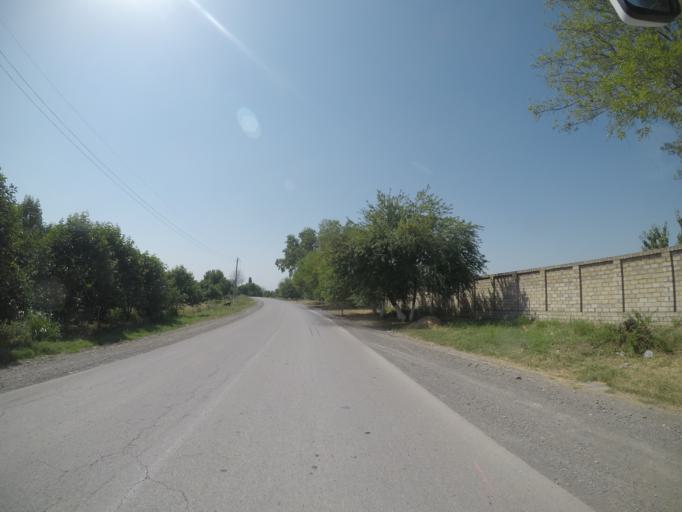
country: AZ
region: Agdas
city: Agdas
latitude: 40.7054
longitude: 47.5395
